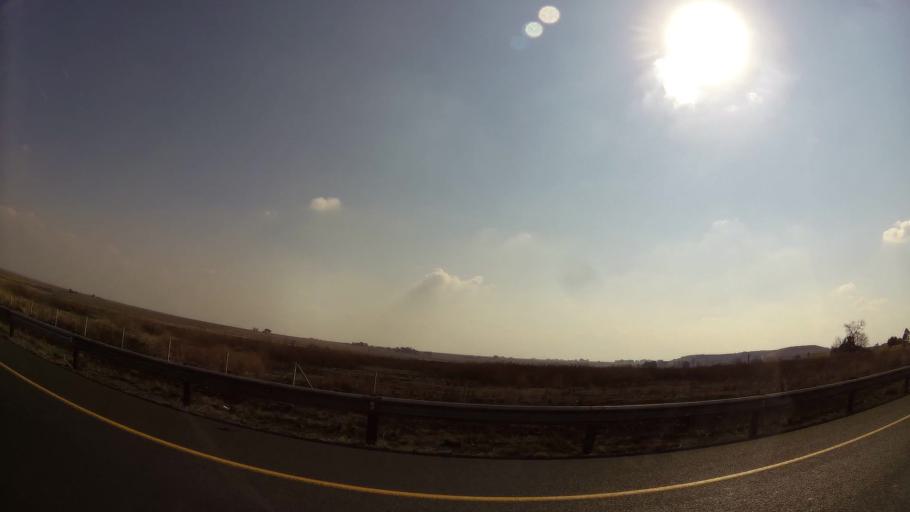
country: ZA
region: Gauteng
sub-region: Ekurhuleni Metropolitan Municipality
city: Springs
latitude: -26.1621
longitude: 28.5159
